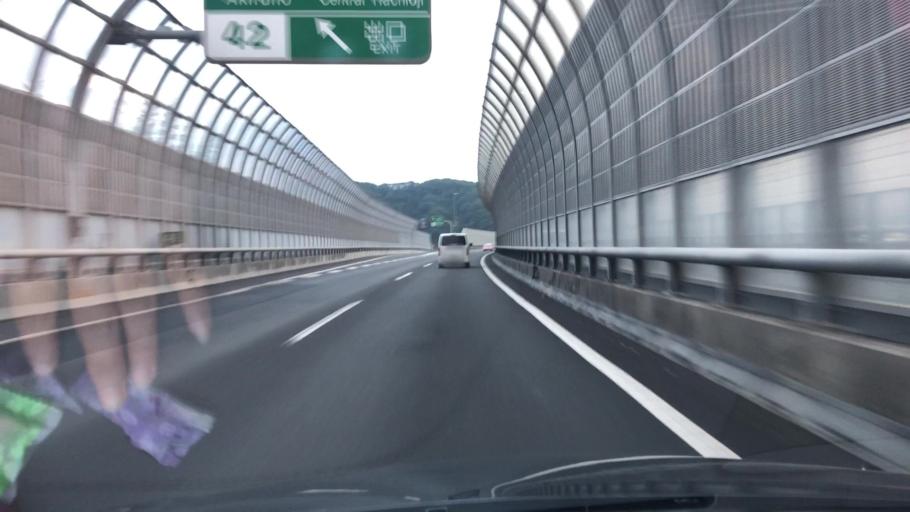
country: JP
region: Tokyo
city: Fussa
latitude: 35.7207
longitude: 139.2841
